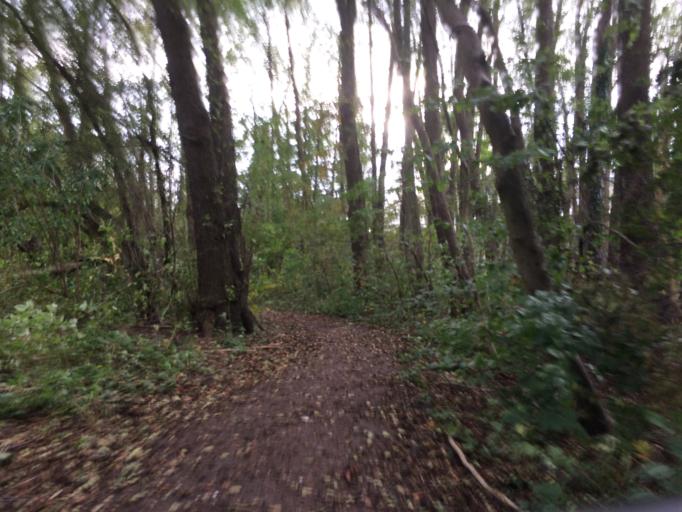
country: DE
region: Berlin
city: Blankenfelde
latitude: 52.6907
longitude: 13.3777
